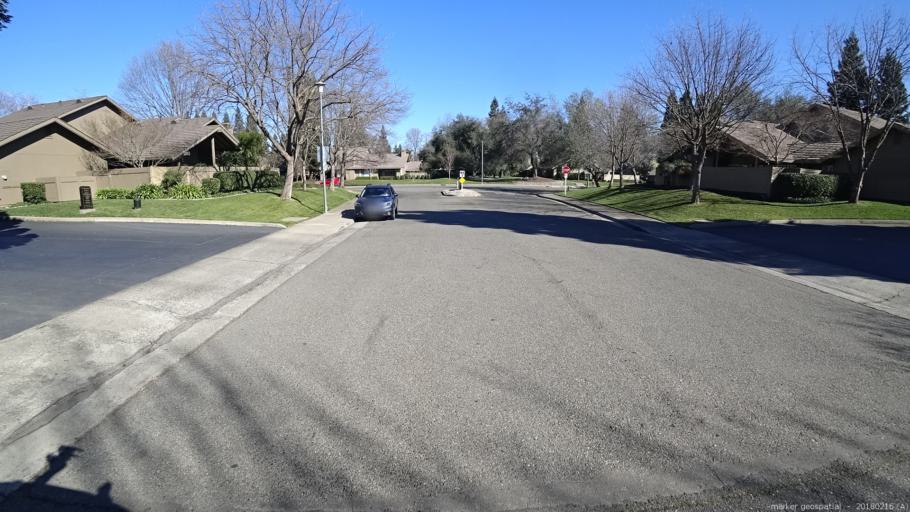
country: US
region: California
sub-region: Sacramento County
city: Gold River
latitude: 38.6236
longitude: -121.2483
